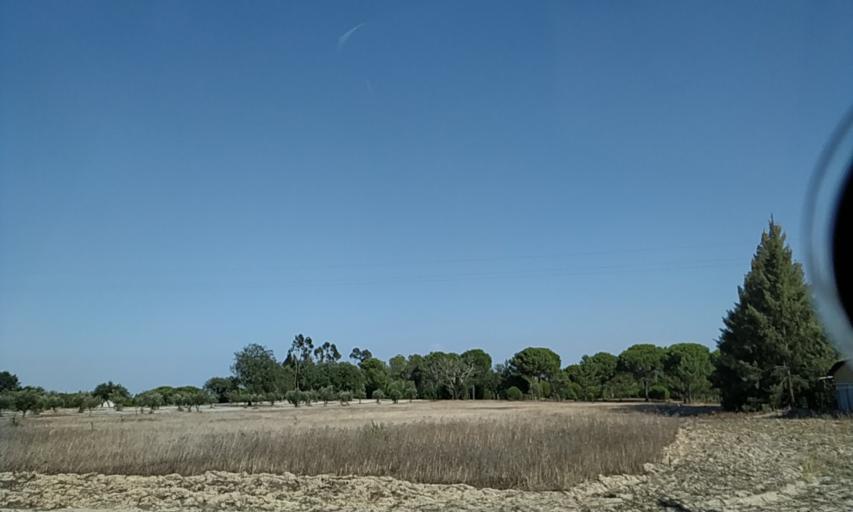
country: PT
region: Santarem
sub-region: Coruche
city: Coruche
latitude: 38.8187
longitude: -8.5703
